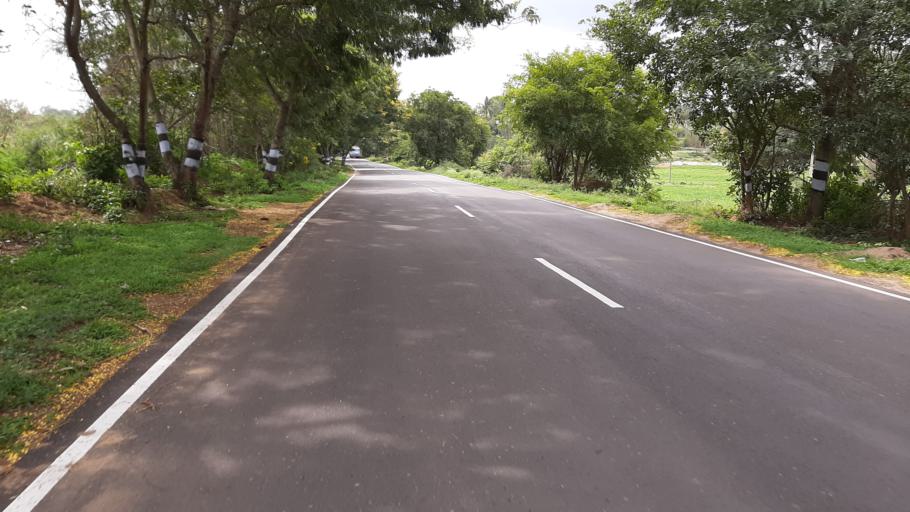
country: IN
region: Tamil Nadu
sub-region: Krishnagiri
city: Denkanikota
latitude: 12.5397
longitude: 77.7647
